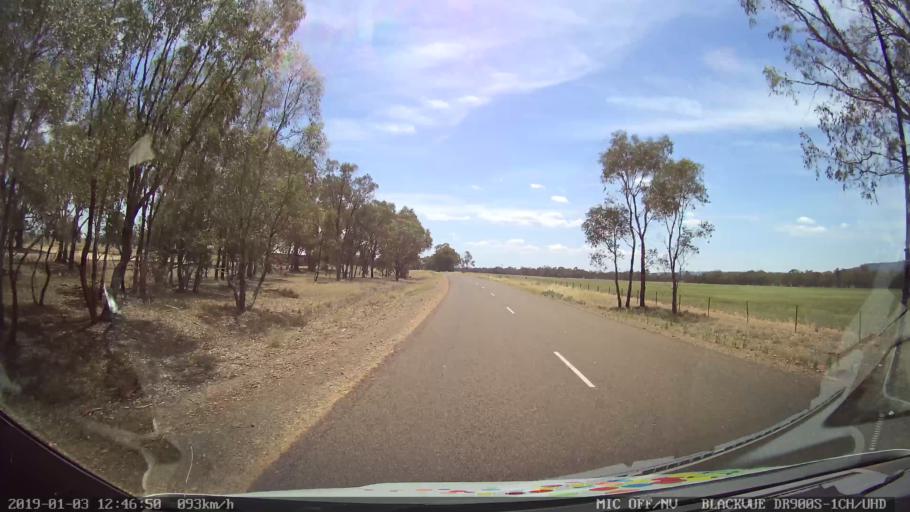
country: AU
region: New South Wales
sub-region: Weddin
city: Grenfell
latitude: -33.7347
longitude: 148.2385
